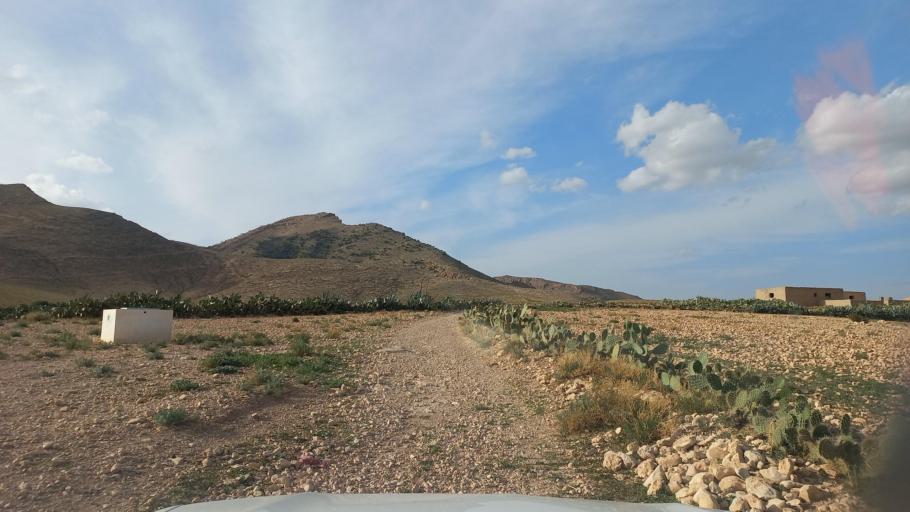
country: TN
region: Al Qasrayn
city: Sbiba
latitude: 35.4574
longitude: 9.0773
